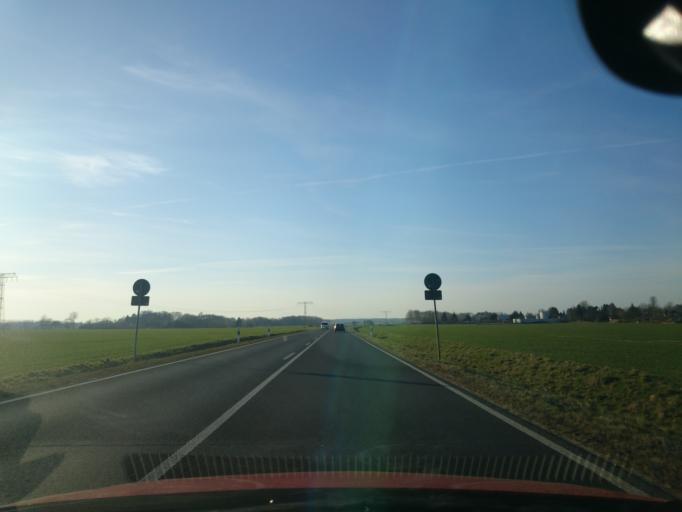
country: DE
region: Mecklenburg-Vorpommern
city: Mesekenhagen
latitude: 54.1436
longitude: 13.3234
